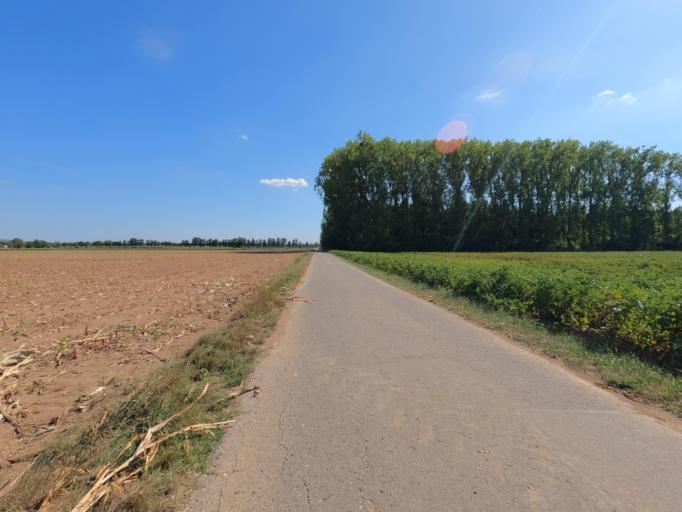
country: DE
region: North Rhine-Westphalia
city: Julich
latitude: 50.9376
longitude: 6.3228
